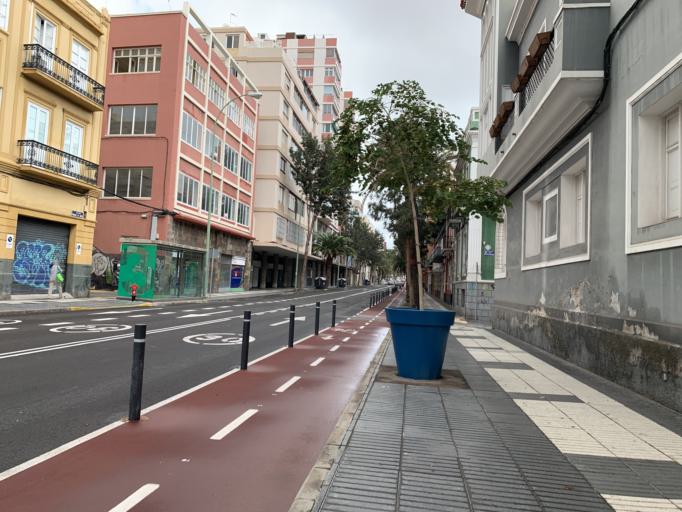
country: ES
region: Canary Islands
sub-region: Provincia de Las Palmas
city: Las Palmas de Gran Canaria
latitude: 28.1051
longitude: -15.4196
